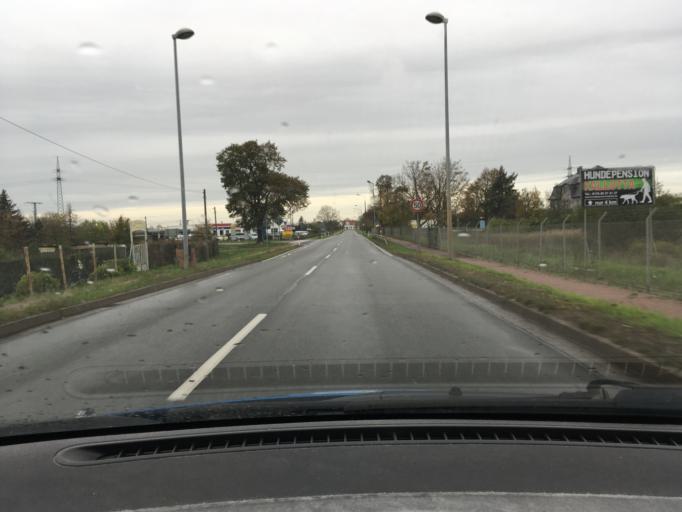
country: DE
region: Saxony-Anhalt
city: Rodleben
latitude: 51.8943
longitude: 12.2215
